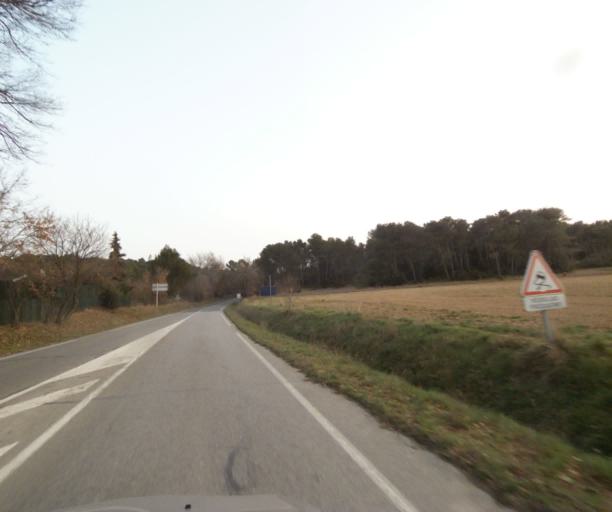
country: FR
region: Provence-Alpes-Cote d'Azur
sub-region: Departement des Bouches-du-Rhone
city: Cabries
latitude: 43.4390
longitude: 5.3621
